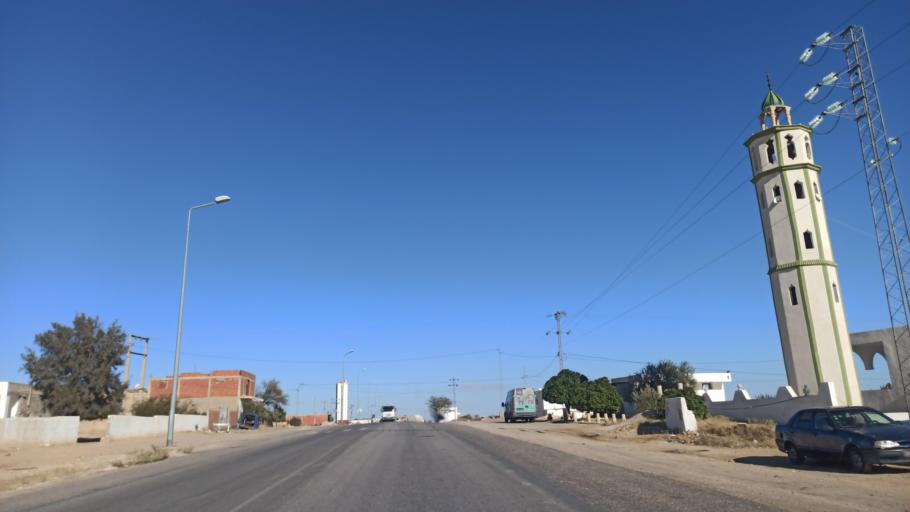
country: TN
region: Sidi Bu Zayd
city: Jilma
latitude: 35.2591
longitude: 9.4038
